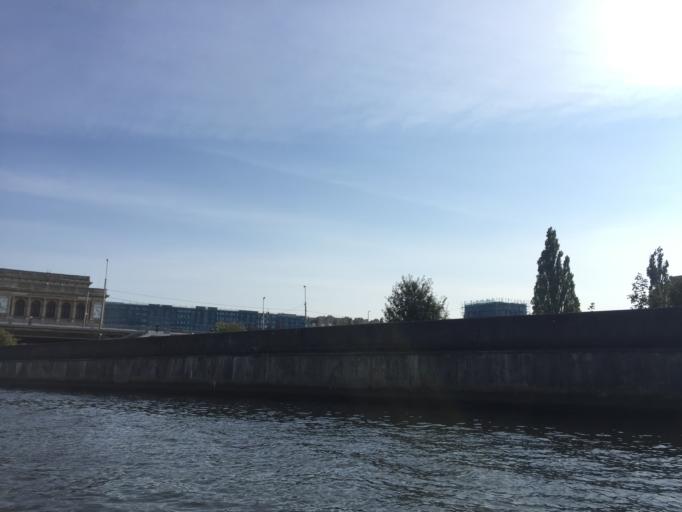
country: RU
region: Kaliningrad
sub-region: Gorod Kaliningrad
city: Kaliningrad
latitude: 54.7056
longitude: 20.5045
